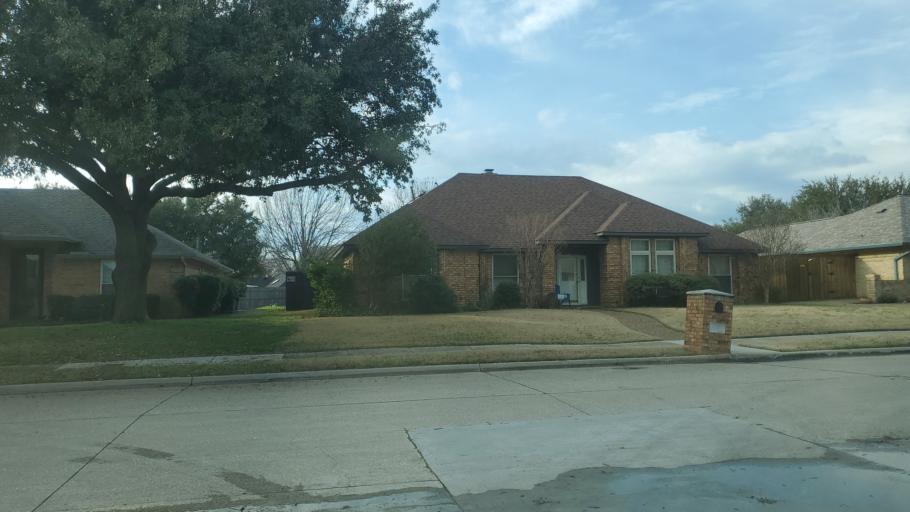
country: US
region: Texas
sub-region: Dallas County
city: Carrollton
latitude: 32.9998
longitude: -96.9004
